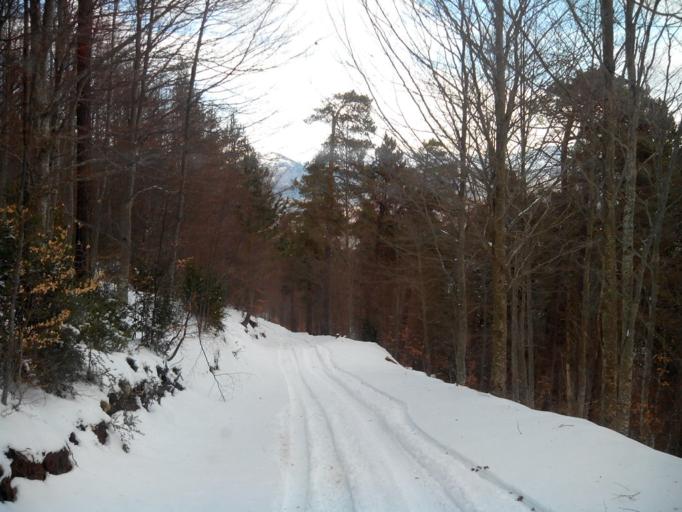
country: ES
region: Catalonia
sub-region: Provincia de Barcelona
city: Sant Julia de Cerdanyola
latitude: 42.2076
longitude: 1.9476
